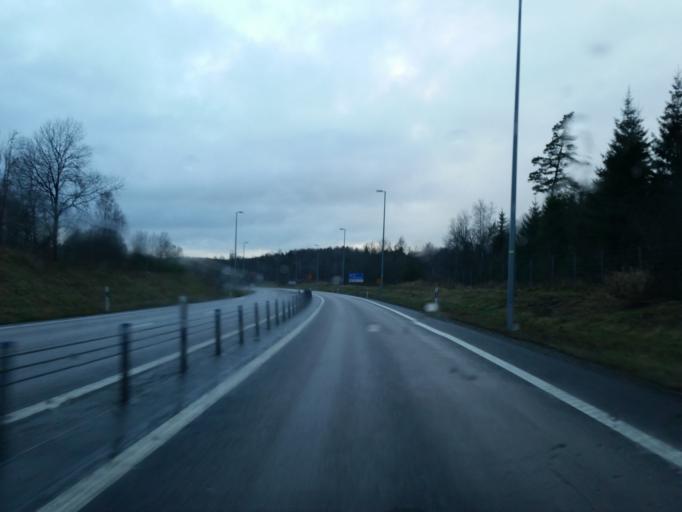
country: SE
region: Vaestra Goetaland
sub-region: Boras Kommun
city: Boras
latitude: 57.6797
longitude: 12.9680
